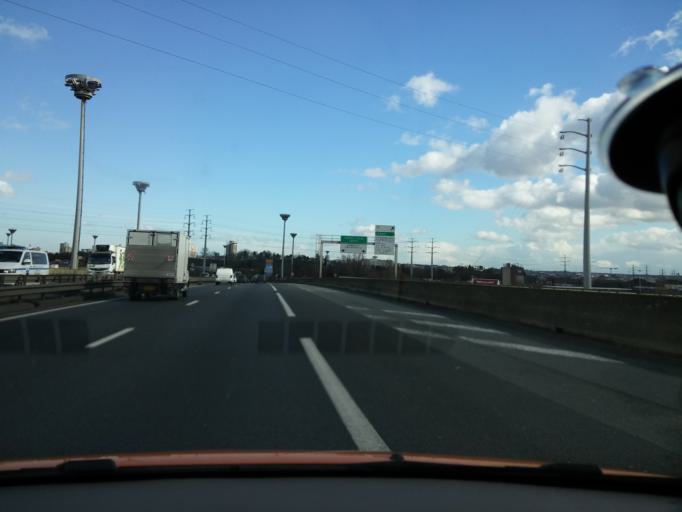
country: FR
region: Ile-de-France
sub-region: Departement du Val-de-Marne
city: Choisy-le-Roi
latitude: 48.7762
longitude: 2.4343
